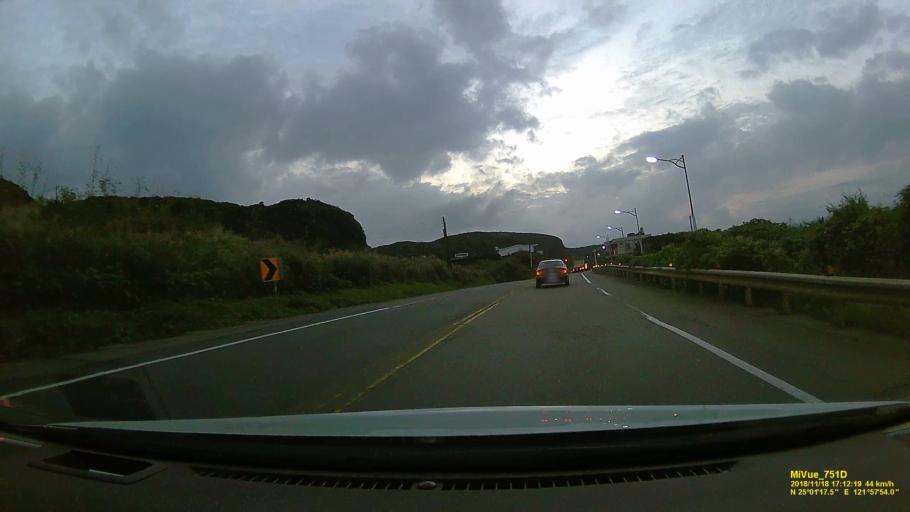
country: TW
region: Taiwan
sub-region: Keelung
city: Keelung
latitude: 25.0215
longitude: 121.9649
